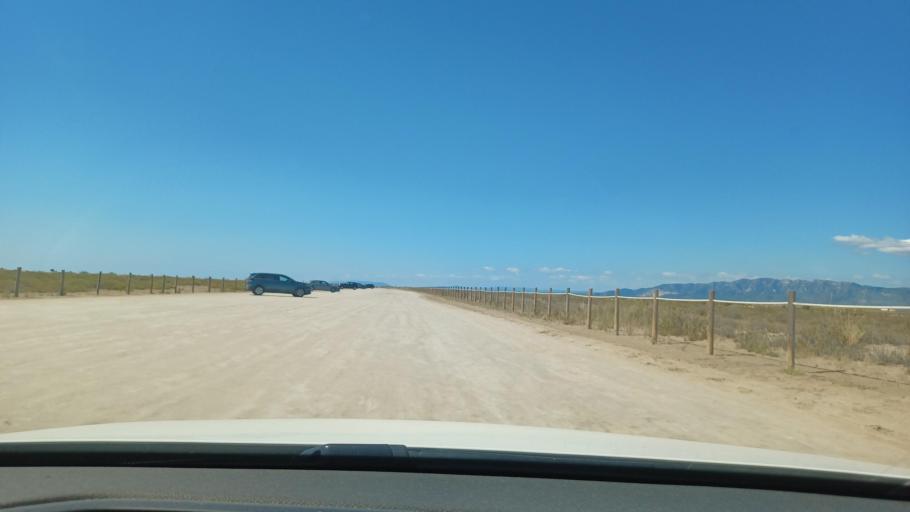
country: ES
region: Catalonia
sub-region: Provincia de Tarragona
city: Deltebre
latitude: 40.6446
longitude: 0.7597
